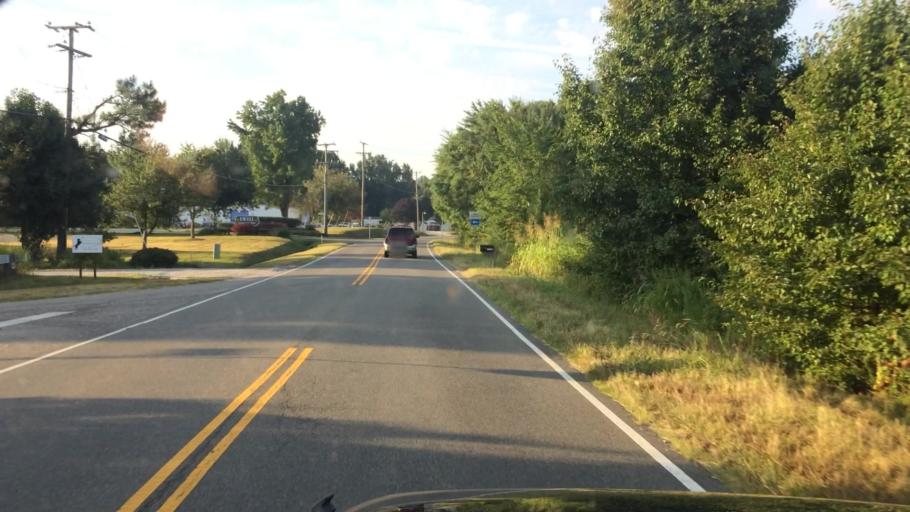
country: US
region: Virginia
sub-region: James City County
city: Williamsburg
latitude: 37.3212
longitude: -76.7349
